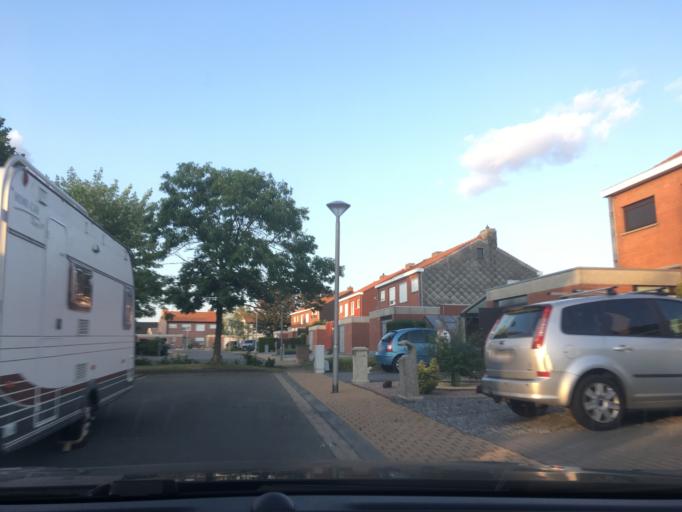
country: BE
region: Flanders
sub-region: Provincie West-Vlaanderen
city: Roeselare
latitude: 50.9262
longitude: 3.1625
